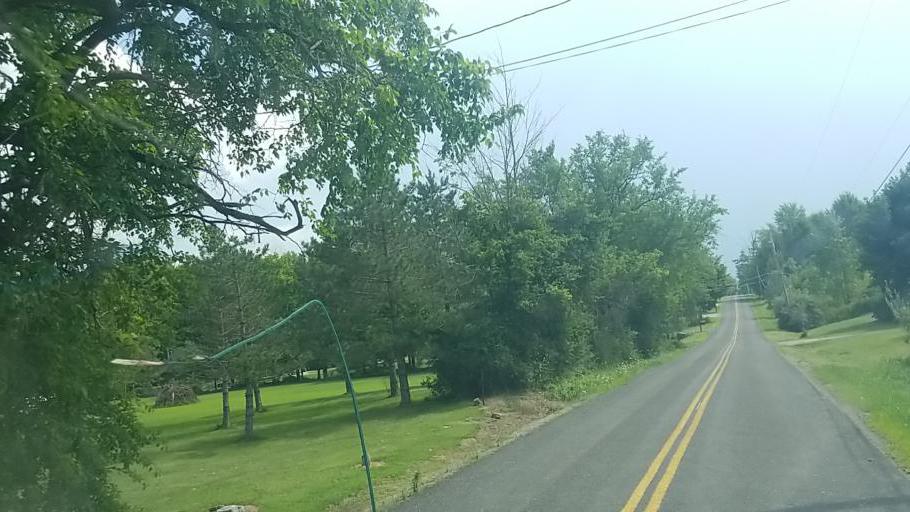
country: US
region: Ohio
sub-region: Medina County
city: Westfield Center
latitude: 41.1193
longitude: -81.9625
